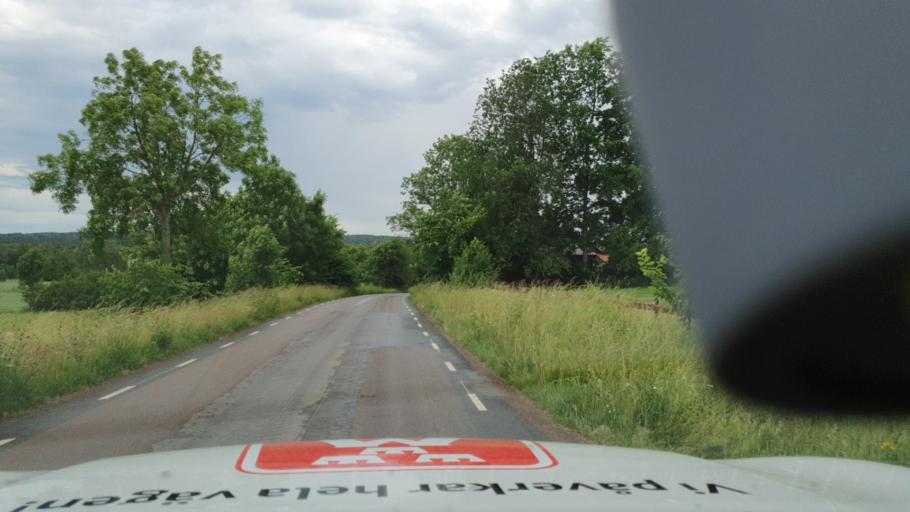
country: SE
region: Vaestra Goetaland
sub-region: Skovde Kommun
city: Stopen
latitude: 58.4999
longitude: 13.7750
